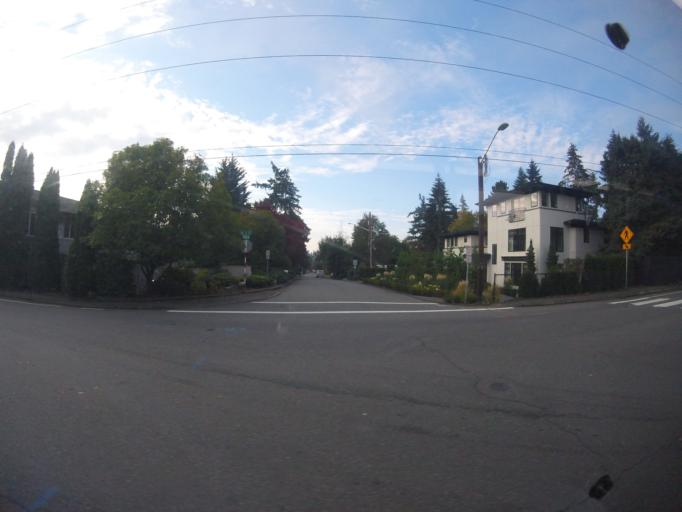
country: US
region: Washington
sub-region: King County
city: Bellevue
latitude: 47.6174
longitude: -122.2091
